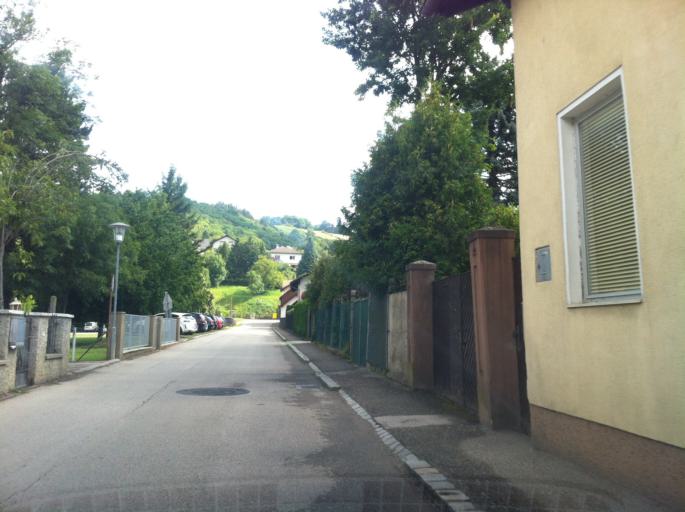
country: AT
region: Lower Austria
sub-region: Politischer Bezirk Tulln
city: Sieghartskirchen
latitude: 48.2541
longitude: 16.0166
